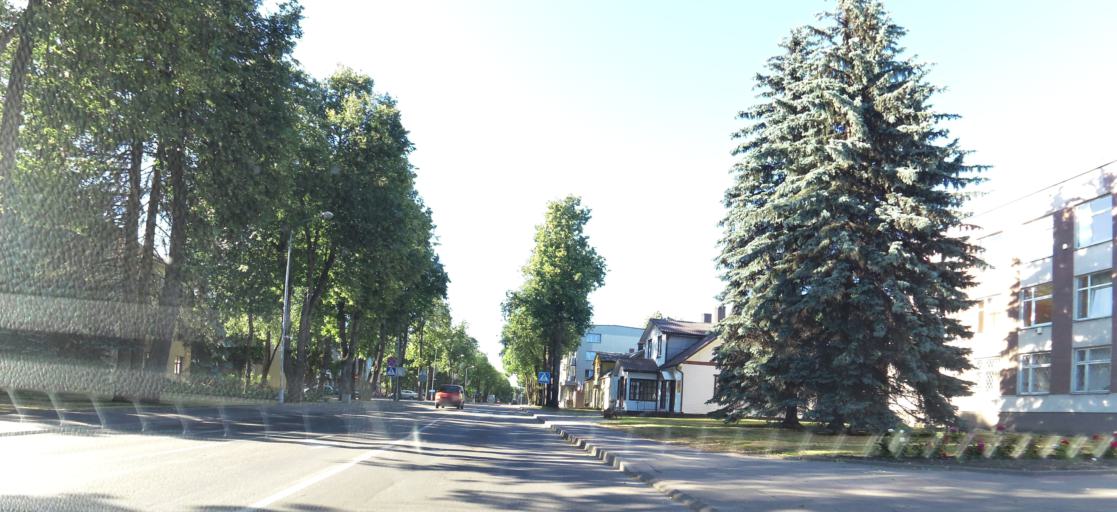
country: LT
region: Panevezys
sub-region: Birzai
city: Birzai
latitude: 56.1951
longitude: 24.7559
